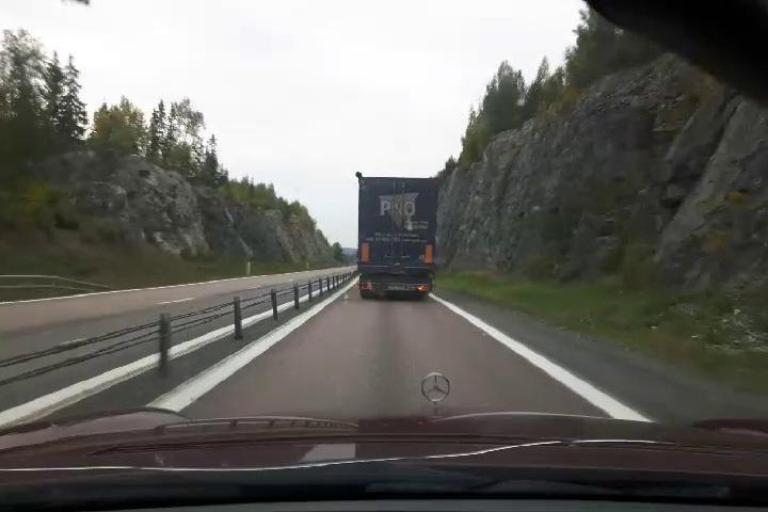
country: SE
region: Vaesternorrland
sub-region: Haernoesands Kommun
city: Haernoesand
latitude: 62.8289
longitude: 17.9681
